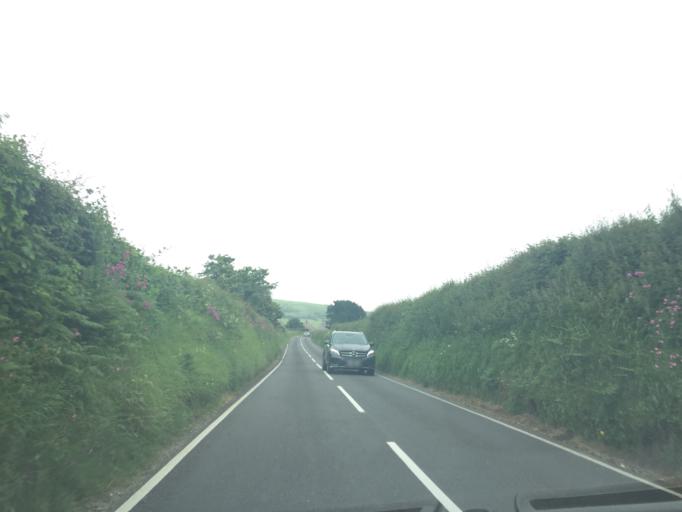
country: GB
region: England
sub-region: Dorset
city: Wool
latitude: 50.6316
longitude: -2.2353
